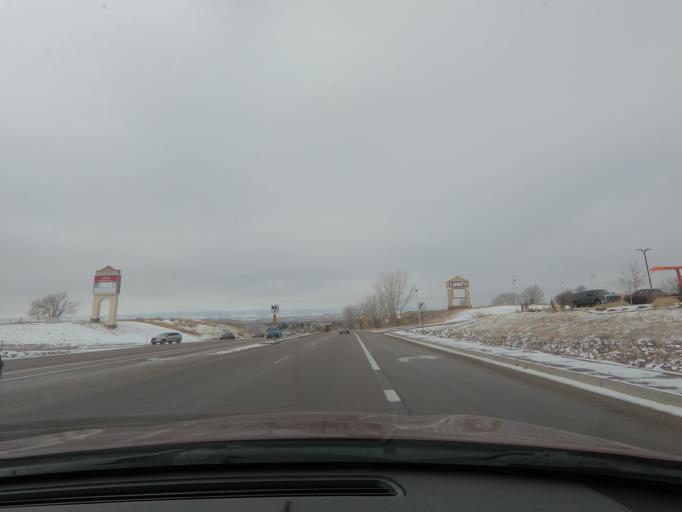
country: US
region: Colorado
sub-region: El Paso County
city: Security-Widefield
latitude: 38.7196
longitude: -104.7022
